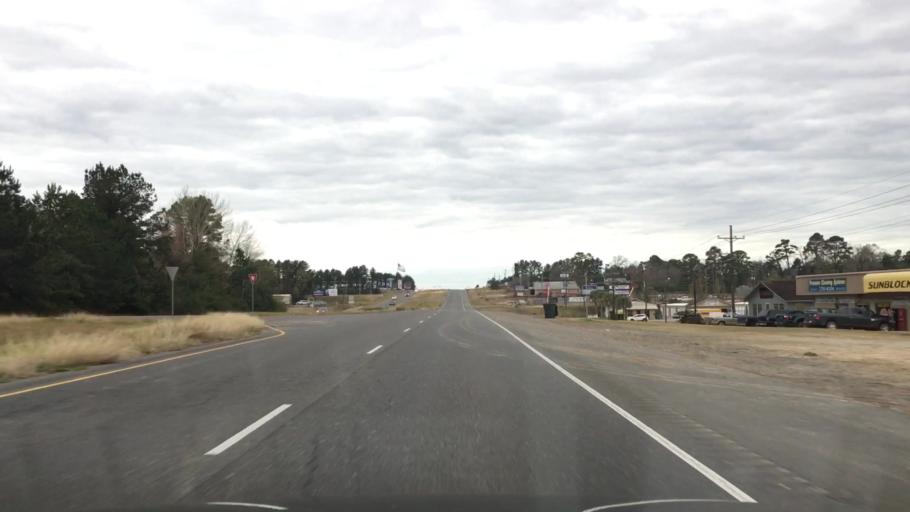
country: US
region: Louisiana
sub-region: Vernon Parish
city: New Llano
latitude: 31.0949
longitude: -93.2701
